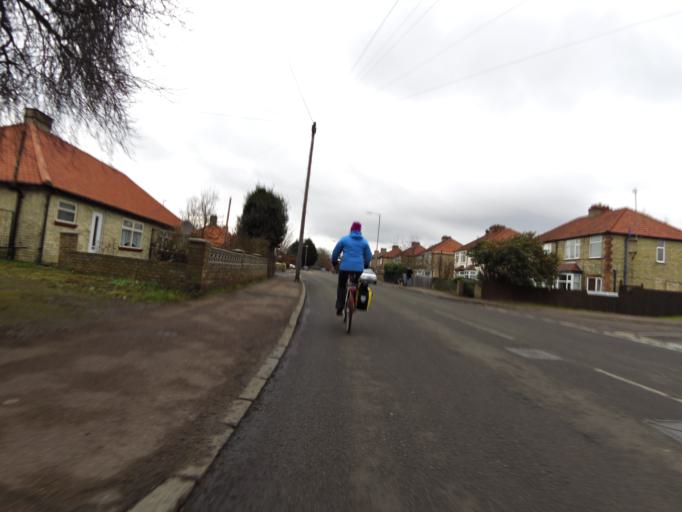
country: GB
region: England
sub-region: Cambridgeshire
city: Cambridge
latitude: 52.2209
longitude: 0.1467
